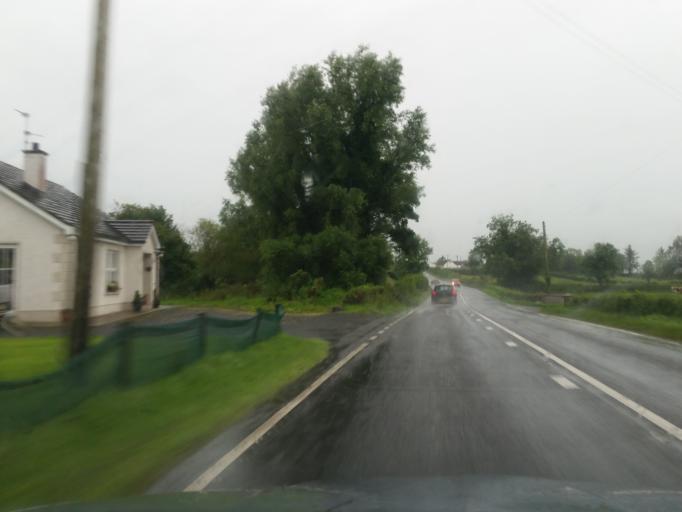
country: GB
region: Northern Ireland
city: Lisnaskea
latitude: 54.2843
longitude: -7.4665
